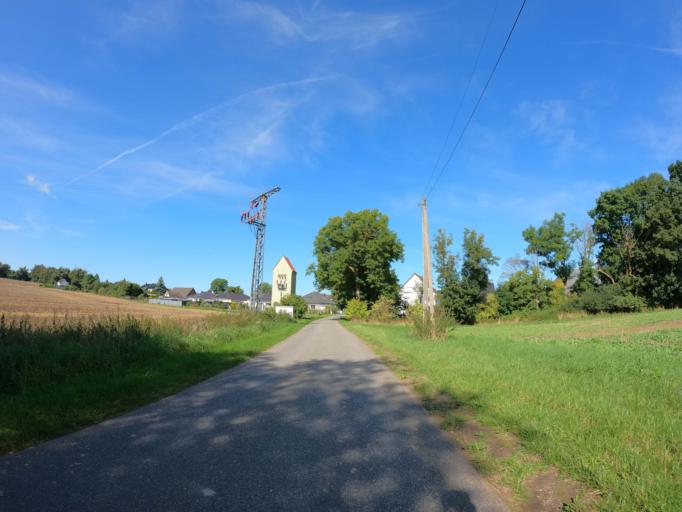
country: DE
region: Mecklenburg-Vorpommern
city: Kramerhof
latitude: 54.3529
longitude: 13.0554
